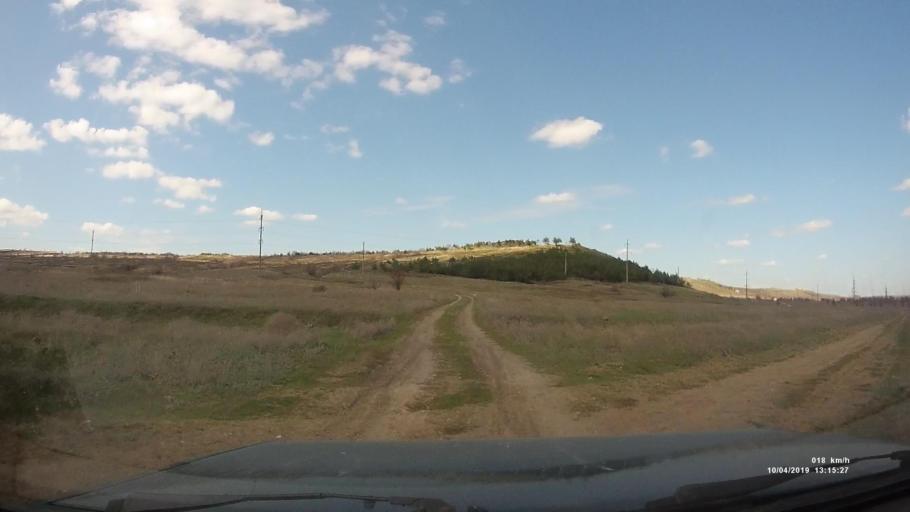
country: RU
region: Rostov
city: Masalovka
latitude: 48.4173
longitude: 40.2586
